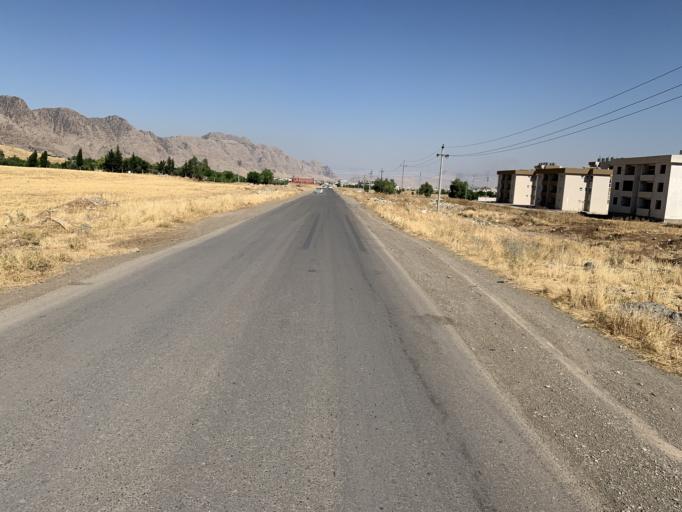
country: IQ
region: As Sulaymaniyah
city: Raniye
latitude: 36.2646
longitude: 44.8447
